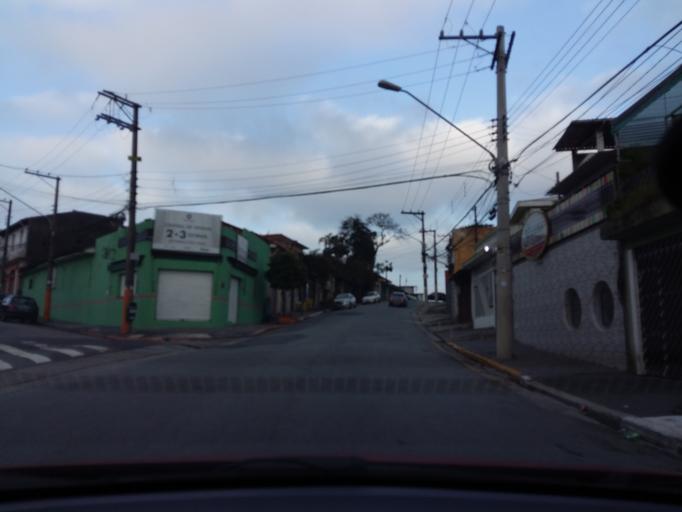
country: BR
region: Sao Paulo
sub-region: Sao Caetano Do Sul
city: Sao Caetano do Sul
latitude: -23.6350
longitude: -46.5910
